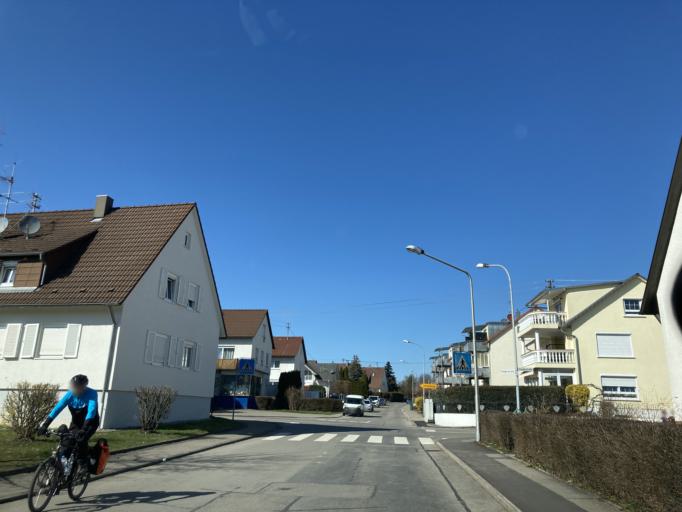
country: DE
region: Baden-Wuerttemberg
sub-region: Tuebingen Region
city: Bodelshausen
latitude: 48.3948
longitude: 8.9771
